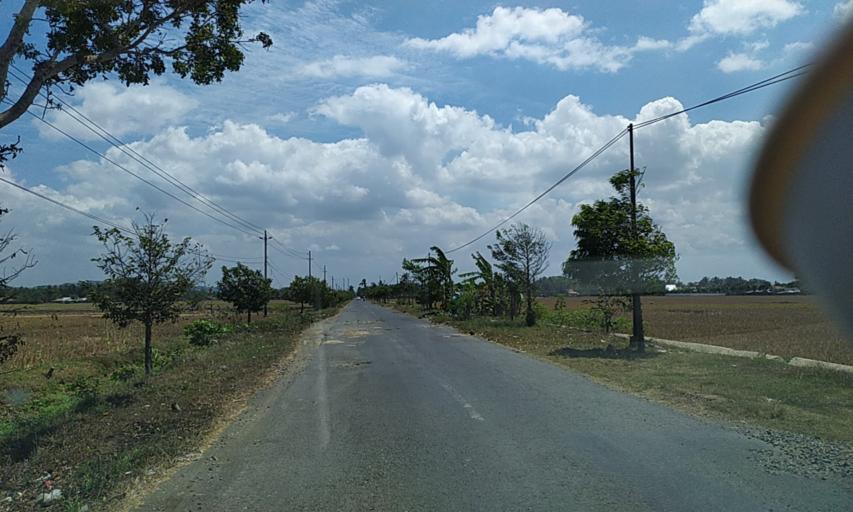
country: ID
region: Central Java
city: Krikil
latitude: -7.6405
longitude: 109.1506
